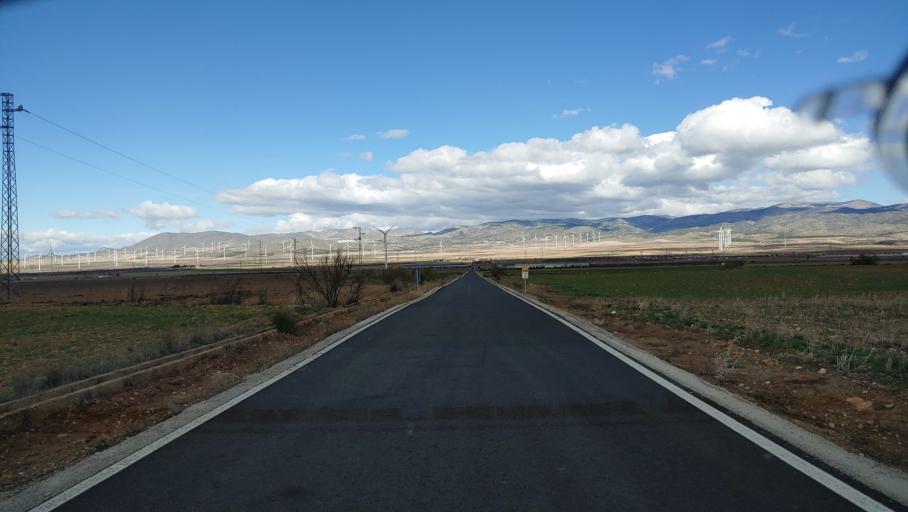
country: ES
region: Andalusia
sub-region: Provincia de Granada
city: Hueneja
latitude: 37.1967
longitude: -2.9540
